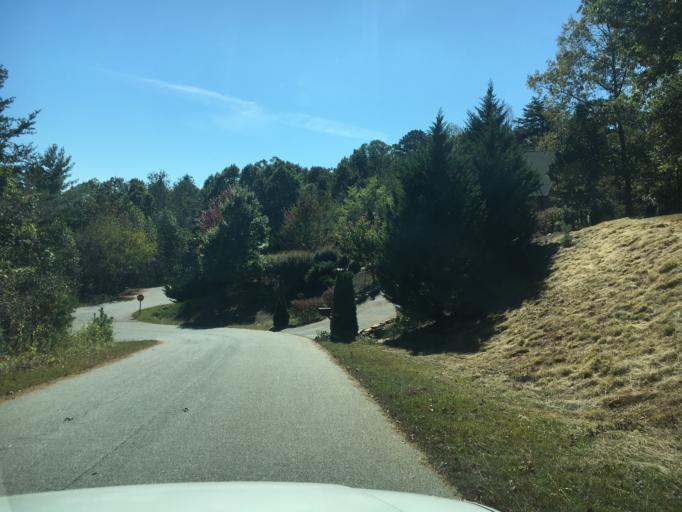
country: US
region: North Carolina
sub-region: Buncombe County
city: Woodfin
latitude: 35.6455
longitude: -82.5865
